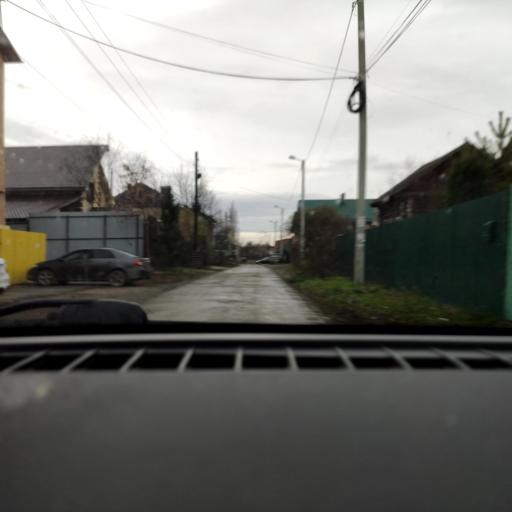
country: RU
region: Perm
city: Kondratovo
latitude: 58.0386
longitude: 56.1174
